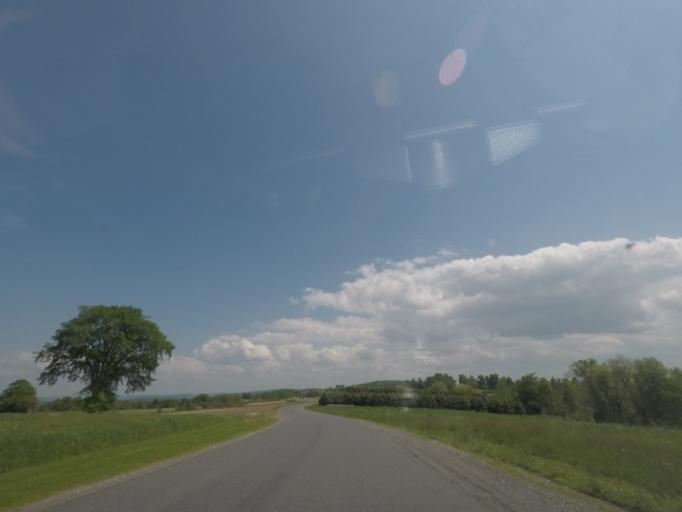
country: US
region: New York
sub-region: Dutchess County
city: Pine Plains
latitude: 41.9767
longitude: -73.5498
